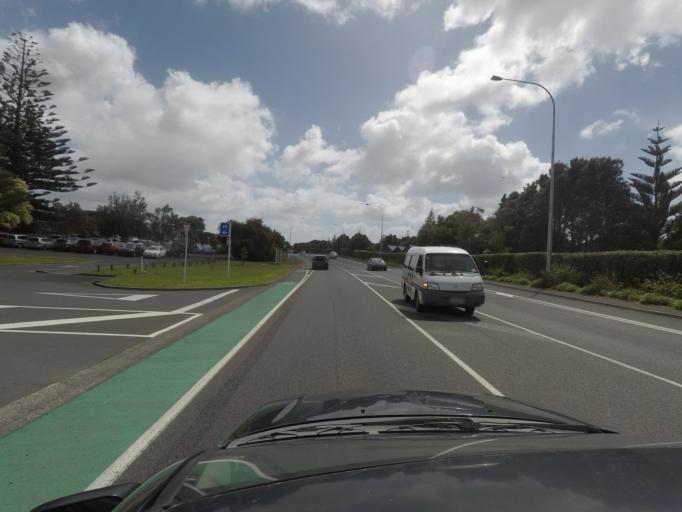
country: NZ
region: Auckland
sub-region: Auckland
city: Rothesay Bay
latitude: -36.5991
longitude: 174.6980
